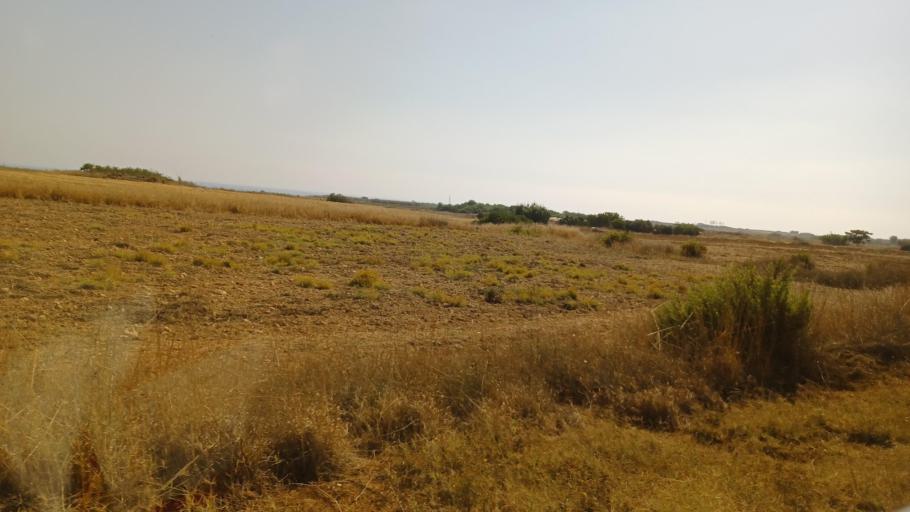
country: CY
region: Ammochostos
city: Paralimni
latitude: 35.0650
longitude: 33.9891
